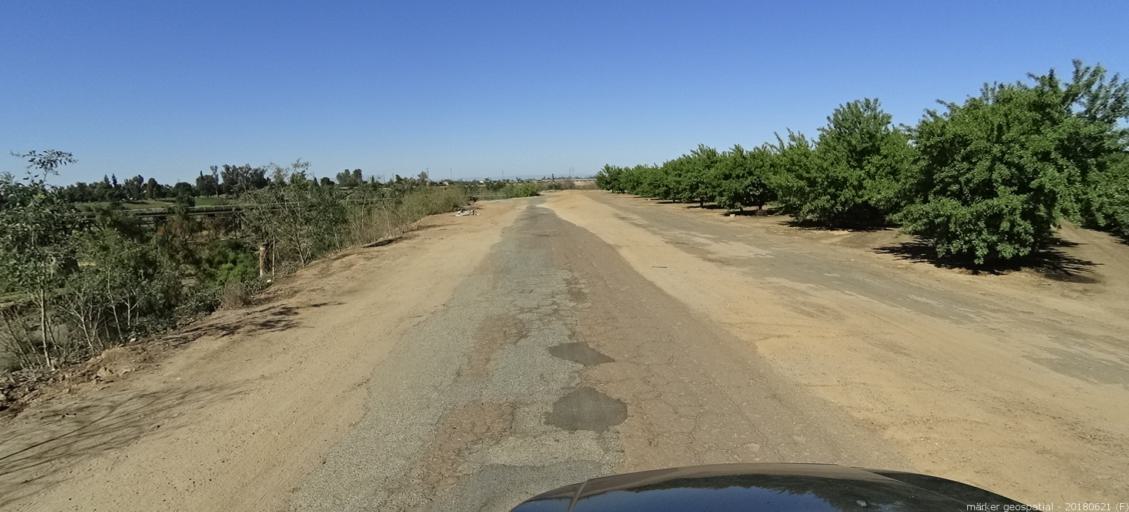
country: US
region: California
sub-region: Fresno County
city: Biola
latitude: 36.8516
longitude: -119.9053
